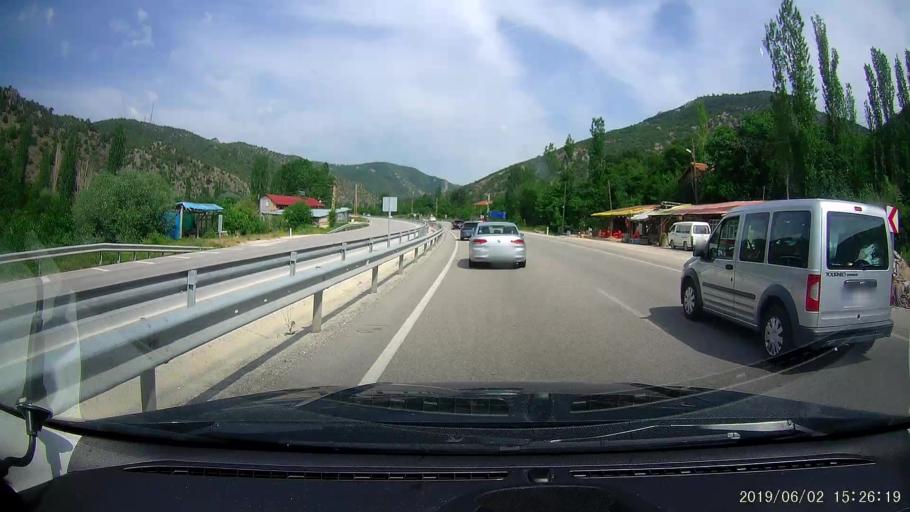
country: TR
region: Amasya
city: Saraycik
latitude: 40.9865
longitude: 35.0339
